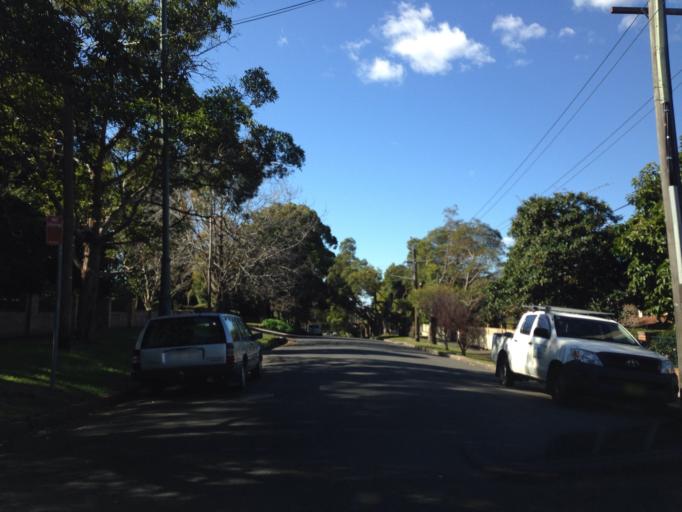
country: AU
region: New South Wales
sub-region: Ku-ring-gai
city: Killara
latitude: -33.7628
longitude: 151.1605
